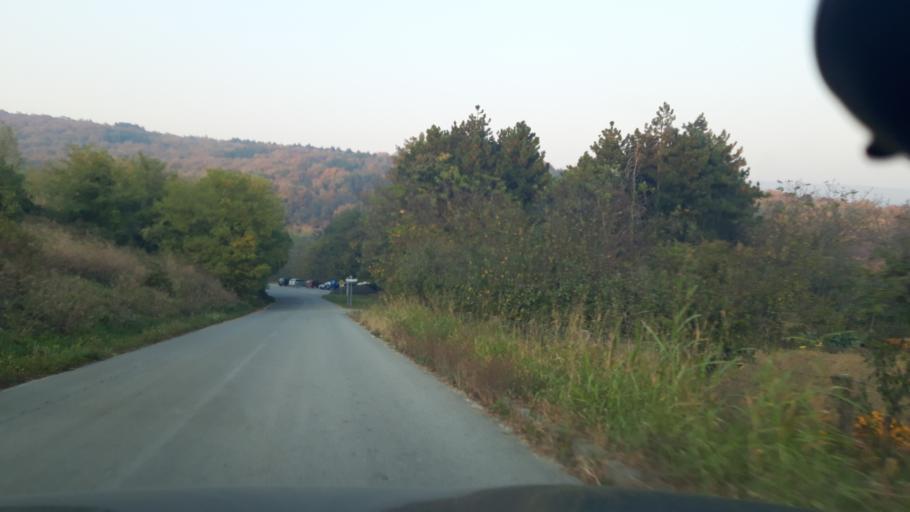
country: RS
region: Autonomna Pokrajina Vojvodina
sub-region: Sremski Okrug
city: Irig
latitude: 45.1260
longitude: 19.8465
